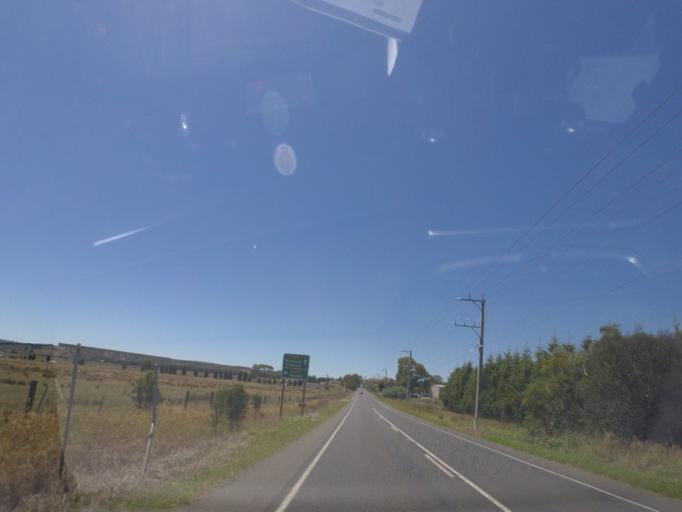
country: AU
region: Victoria
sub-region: Whittlesea
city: Whittlesea
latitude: -37.4239
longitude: 145.0221
